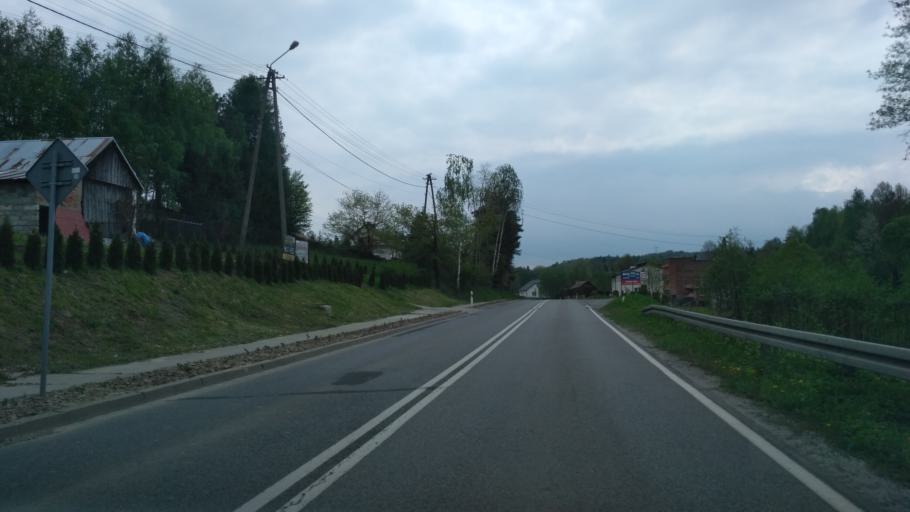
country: PL
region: Lesser Poland Voivodeship
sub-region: Powiat tarnowski
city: Tarnowiec
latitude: 49.9570
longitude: 20.9996
